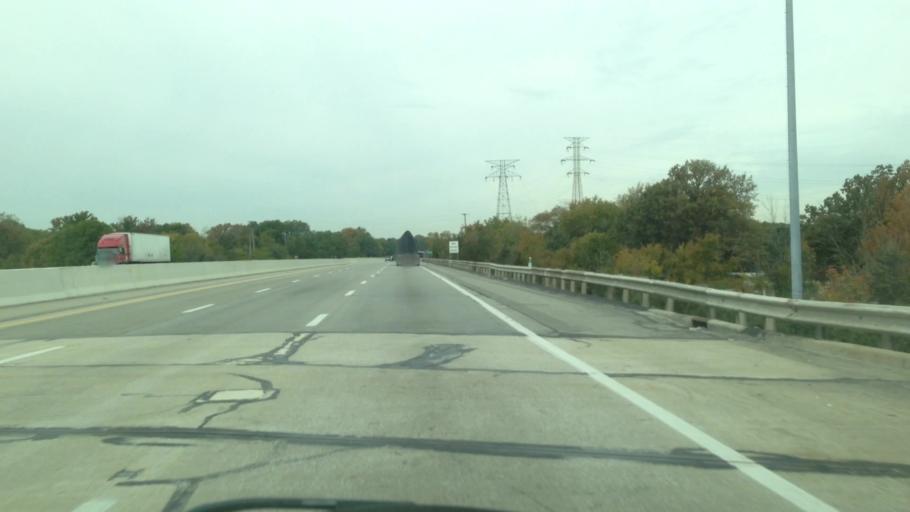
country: US
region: Ohio
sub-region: Wood County
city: Perrysburg
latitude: 41.5764
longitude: -83.5984
